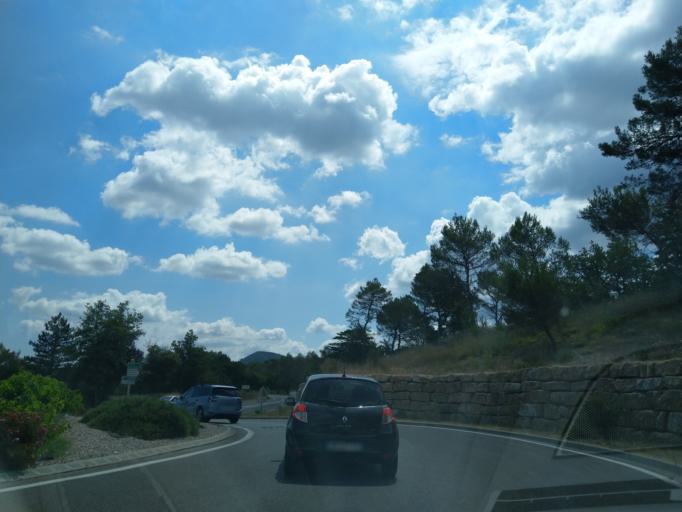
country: FR
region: Provence-Alpes-Cote d'Azur
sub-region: Departement du Var
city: Nans-les-Pins
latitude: 43.3927
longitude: 5.7973
